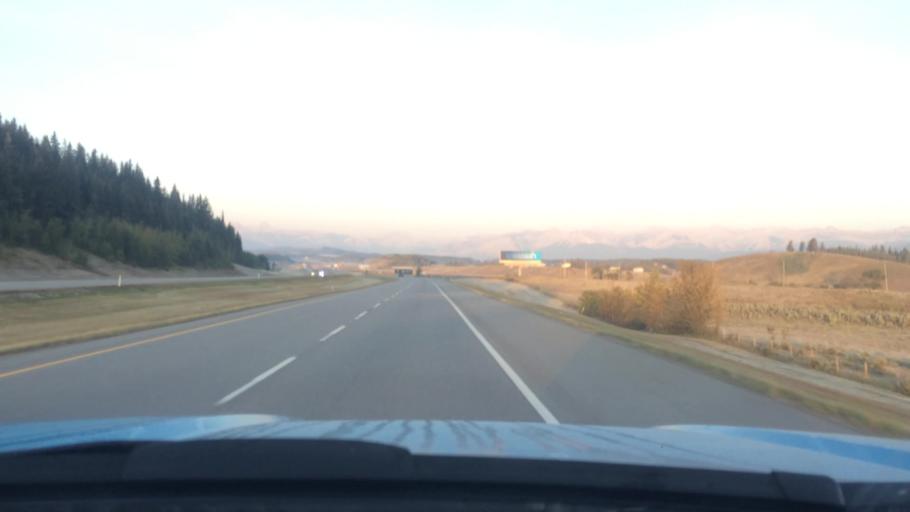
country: CA
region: Alberta
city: Cochrane
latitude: 51.1596
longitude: -114.7867
